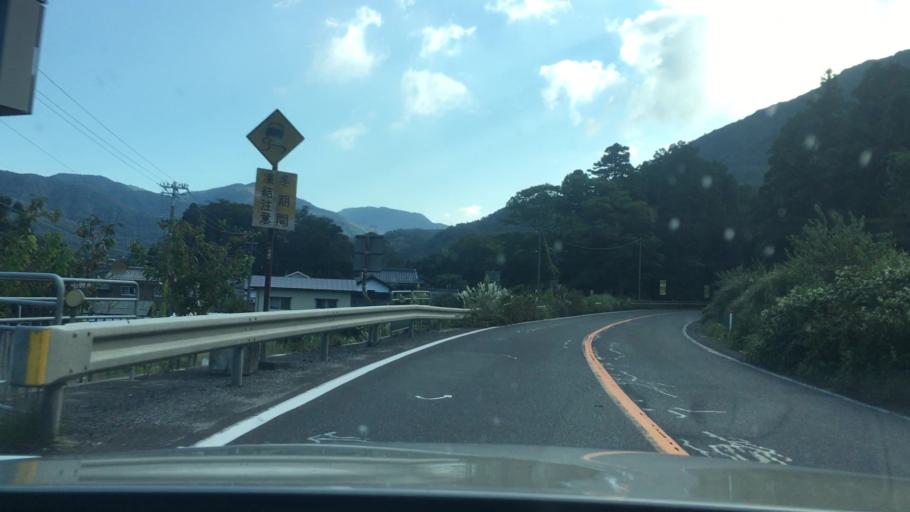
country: JP
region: Fukui
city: Tsuruga
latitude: 35.5932
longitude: 136.1001
